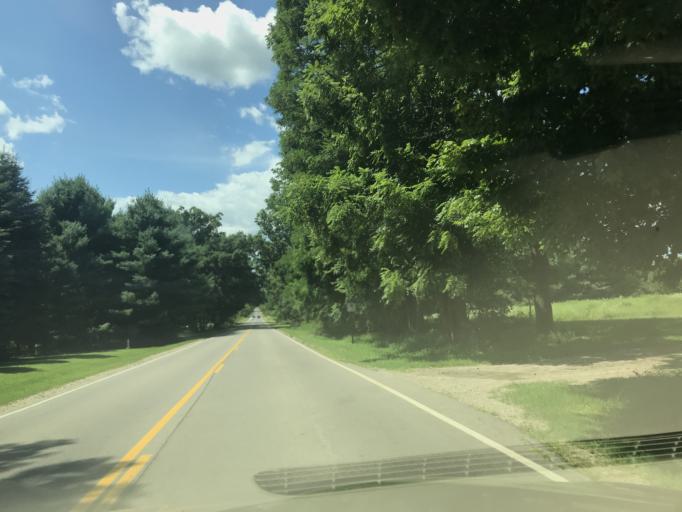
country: US
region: Michigan
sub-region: Ingham County
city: Leslie
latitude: 42.4511
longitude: -84.4834
